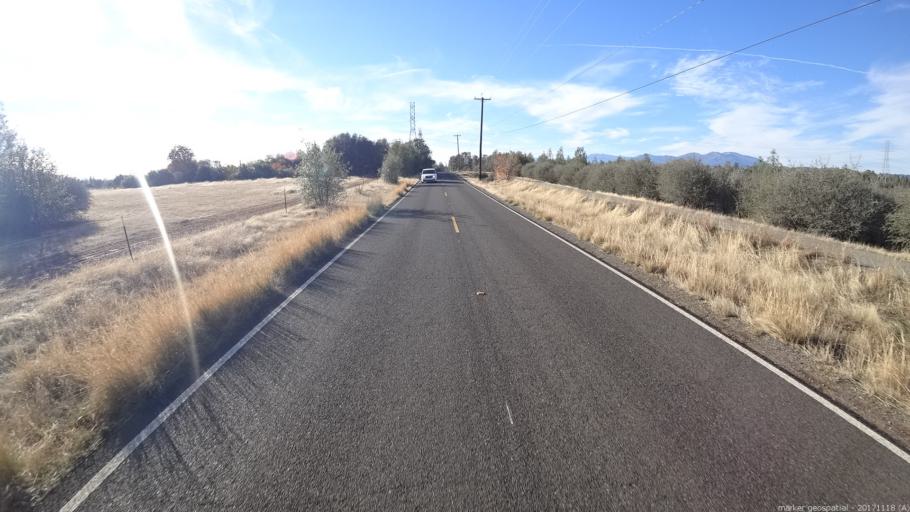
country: US
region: California
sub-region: Shasta County
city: Anderson
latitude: 40.4465
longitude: -122.4132
